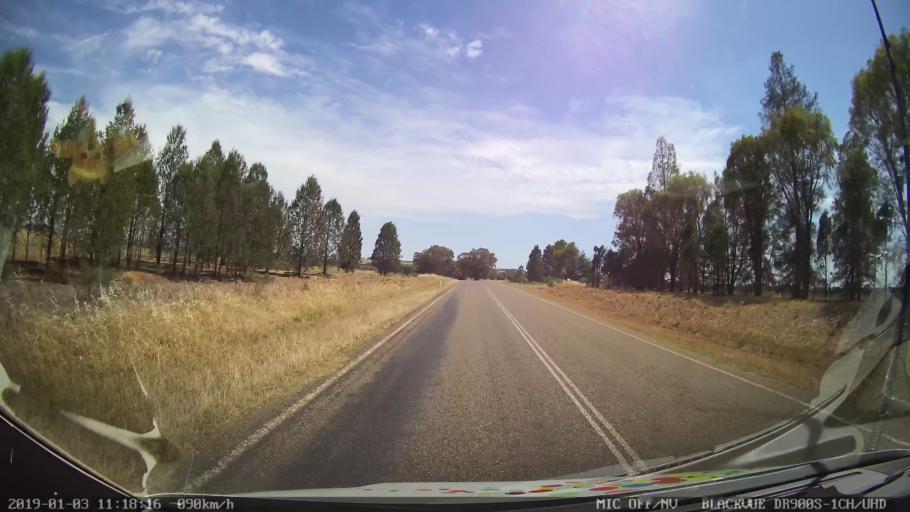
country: AU
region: New South Wales
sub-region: Young
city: Young
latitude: -34.1283
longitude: 148.2633
